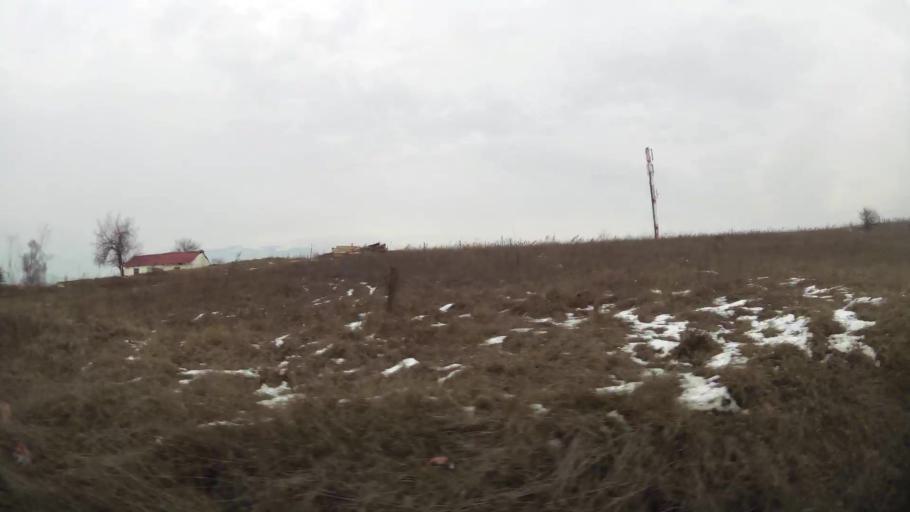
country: MK
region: Butel
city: Butel
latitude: 42.0412
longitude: 21.4386
